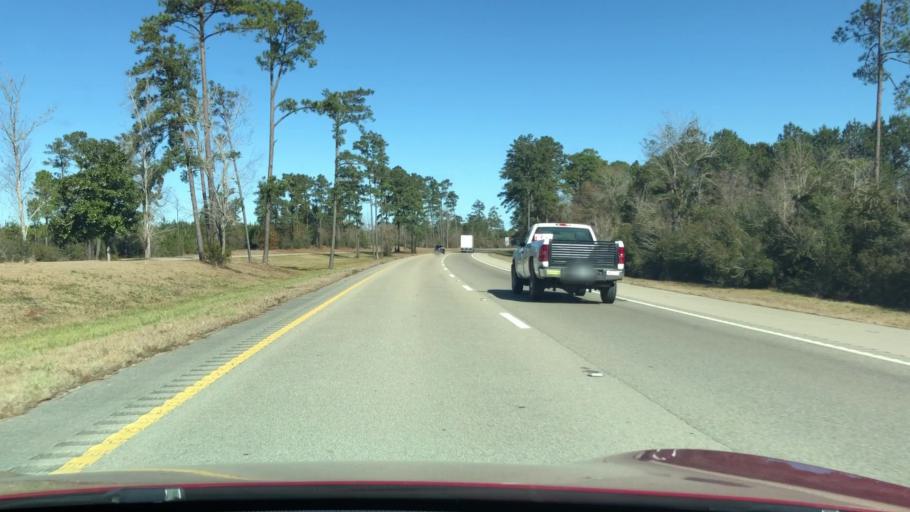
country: US
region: Mississippi
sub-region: Pearl River County
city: Poplarville
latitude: 30.7232
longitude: -89.5520
